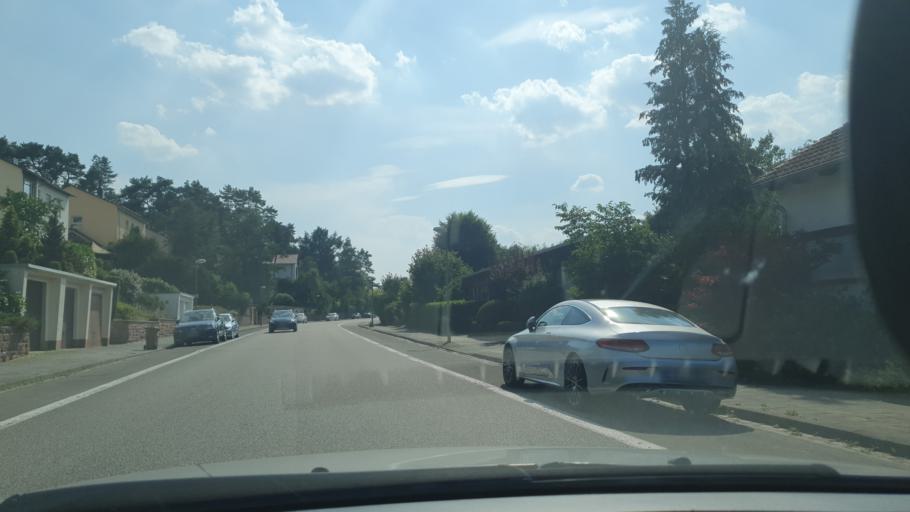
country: DE
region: Rheinland-Pfalz
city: Kaiserslautern
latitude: 49.4366
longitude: 7.7348
